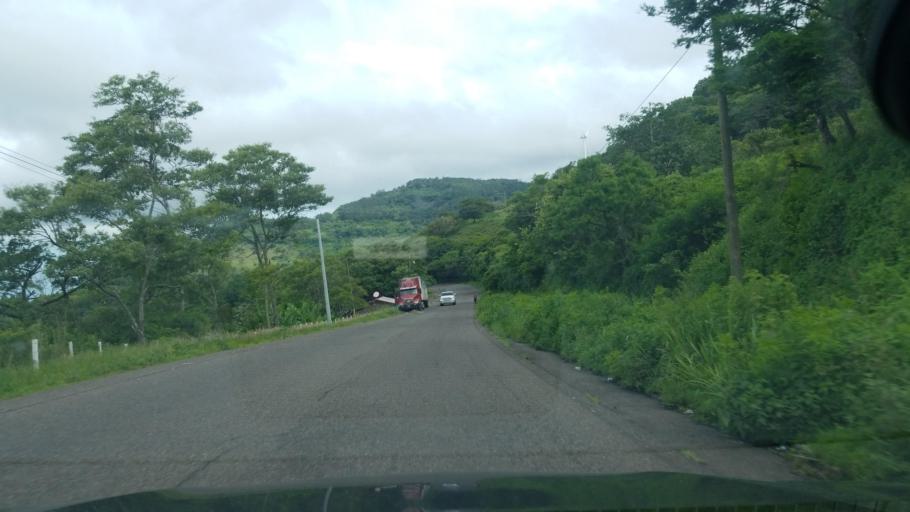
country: HN
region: Choluteca
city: Corpus
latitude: 13.3688
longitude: -86.9349
